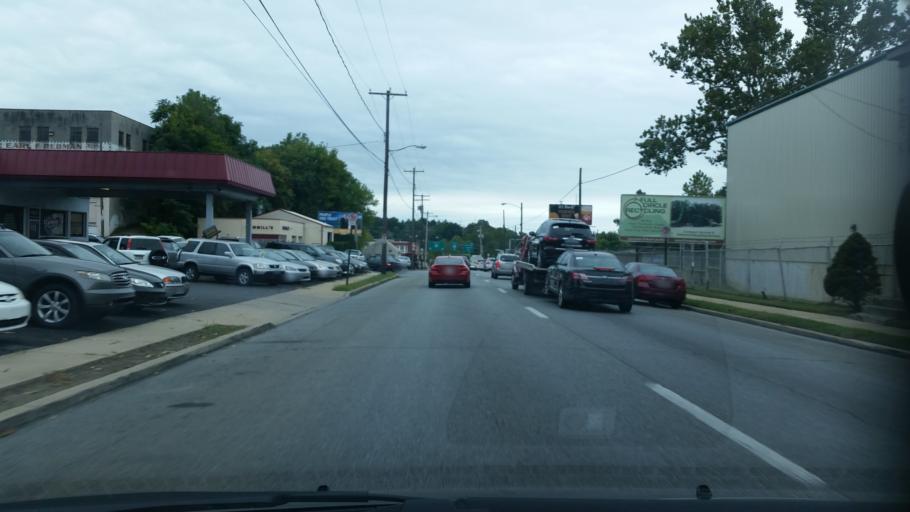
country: US
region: Pennsylvania
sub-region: Lancaster County
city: Lancaster
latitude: 40.0256
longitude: -76.3054
